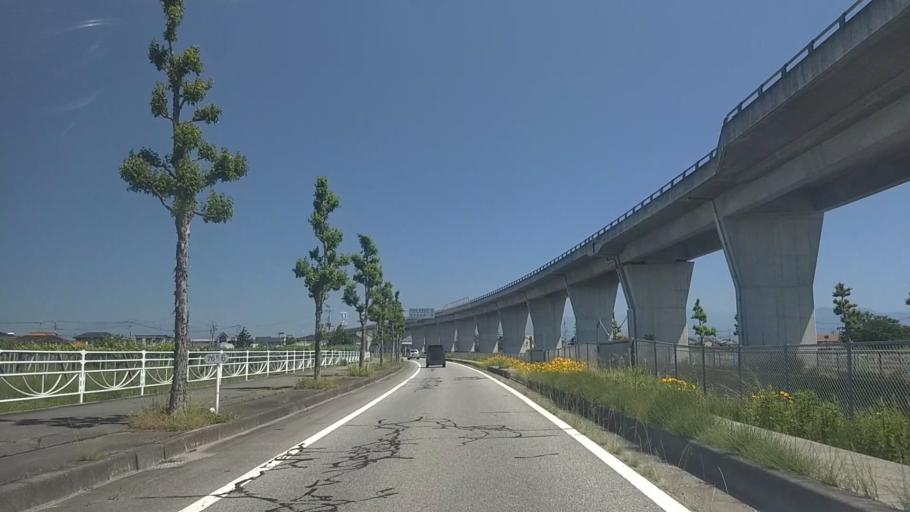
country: JP
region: Yamanashi
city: Ryuo
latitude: 35.6059
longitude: 138.4812
